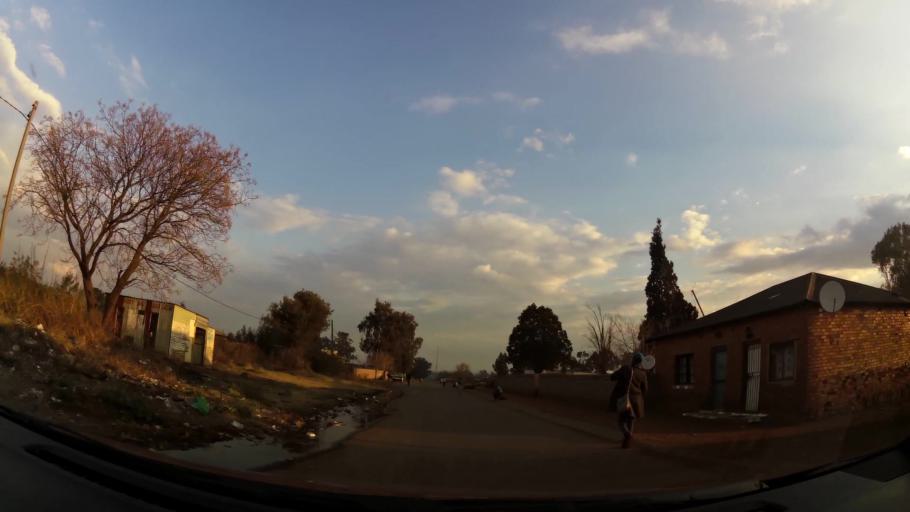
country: ZA
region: Gauteng
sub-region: City of Johannesburg Metropolitan Municipality
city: Orange Farm
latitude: -26.5358
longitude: 27.8509
